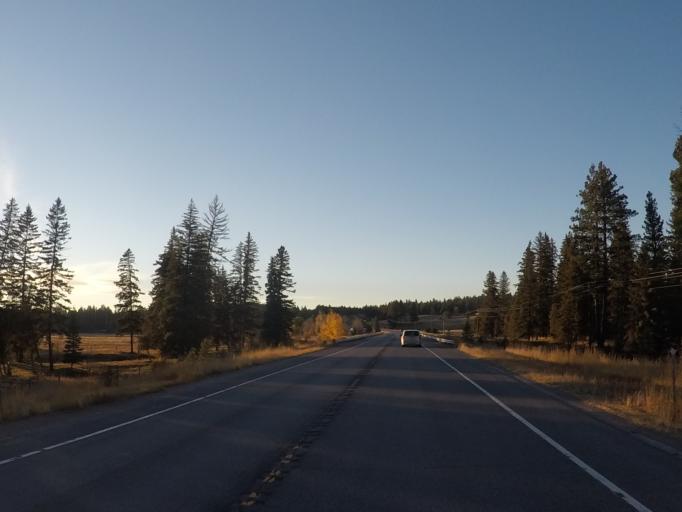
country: US
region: Montana
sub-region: Lewis and Clark County
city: Lincoln
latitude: 47.0040
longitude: -113.0437
